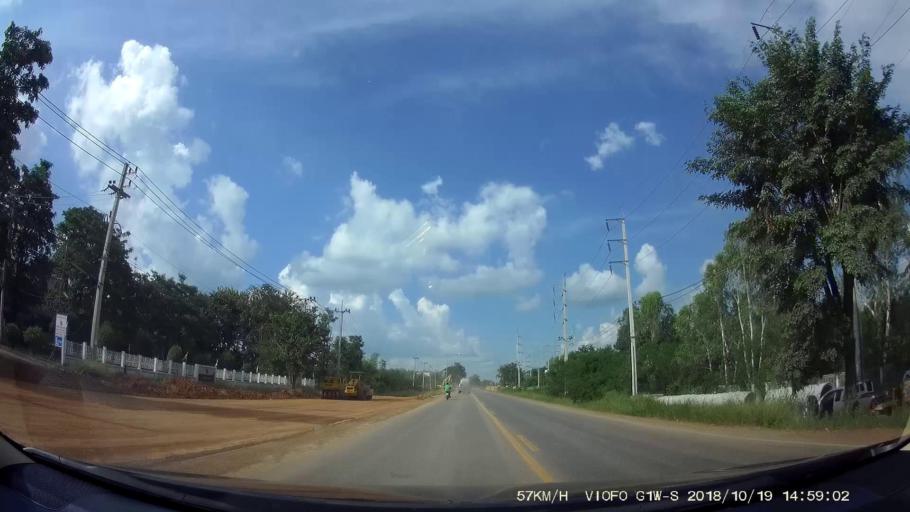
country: TH
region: Chaiyaphum
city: Phu Khiao
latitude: 16.3799
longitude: 102.1293
